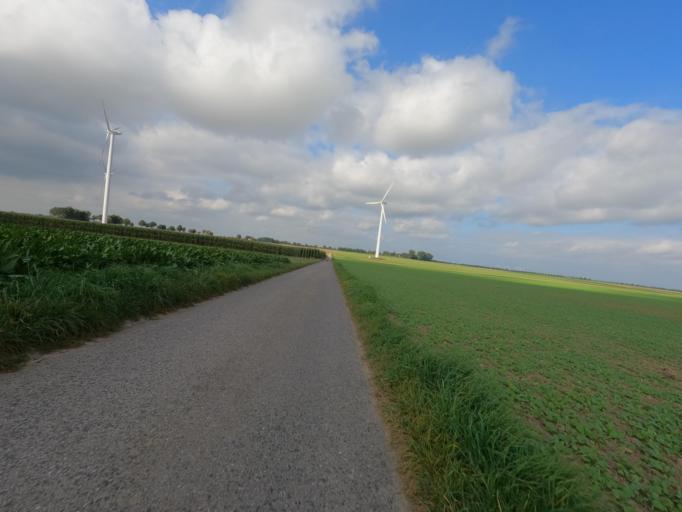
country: DE
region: North Rhine-Westphalia
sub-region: Regierungsbezirk Koln
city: Ubach-Palenberg
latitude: 50.9316
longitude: 6.1407
